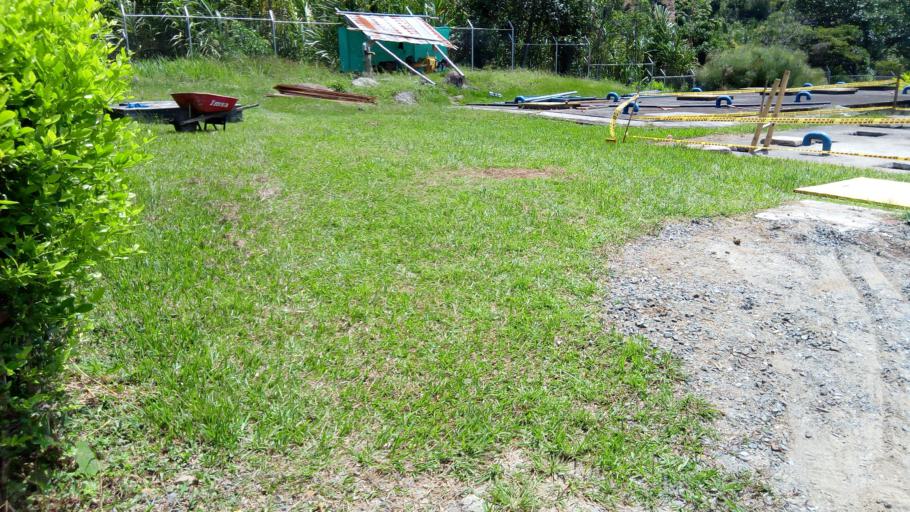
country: CO
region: Valle del Cauca
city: Jamundi
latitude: 3.3467
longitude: -76.5849
